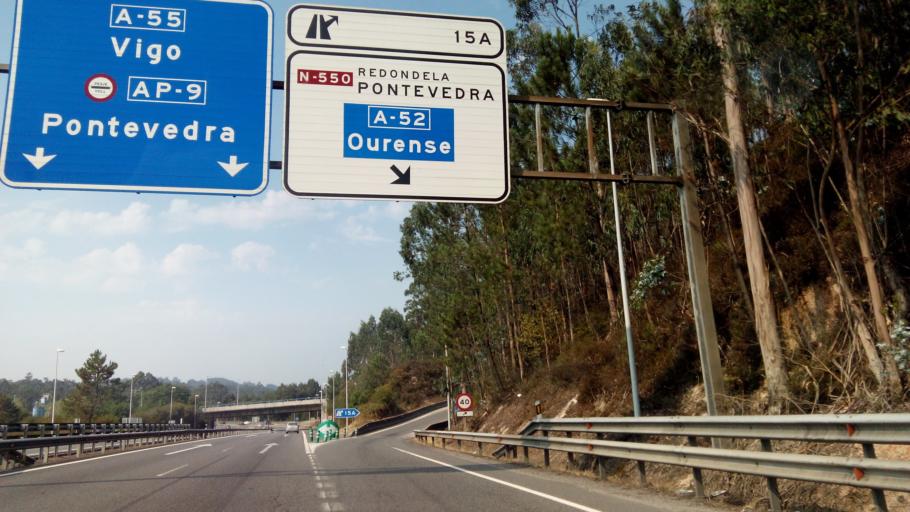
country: ES
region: Galicia
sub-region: Provincia de Pontevedra
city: Porrino
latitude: 42.1689
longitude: -8.6233
